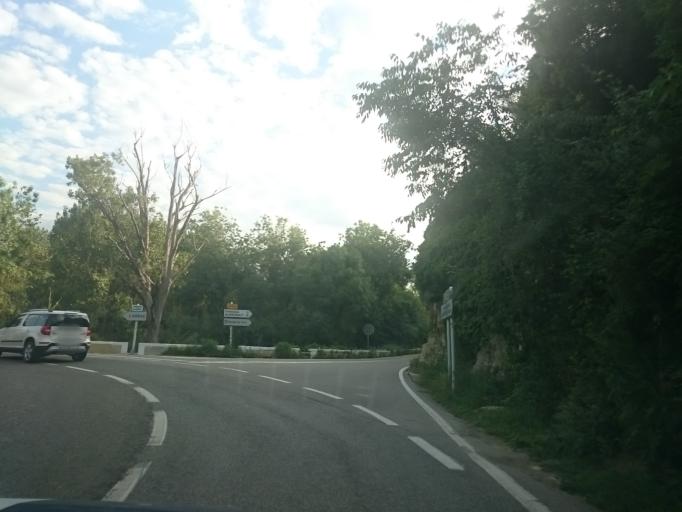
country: ES
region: Catalonia
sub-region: Provincia de Barcelona
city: Castellet
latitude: 41.2634
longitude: 1.6337
